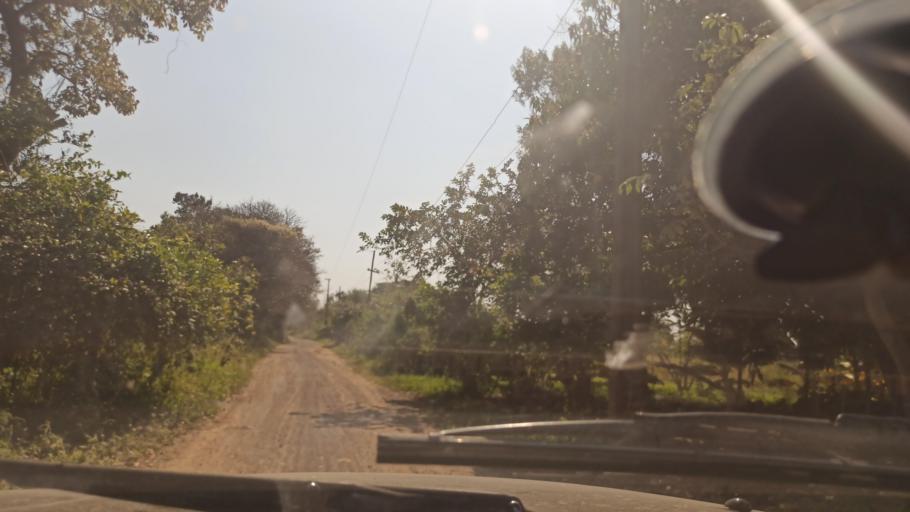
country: AR
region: Formosa
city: Clorinda
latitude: -25.3289
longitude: -57.6911
